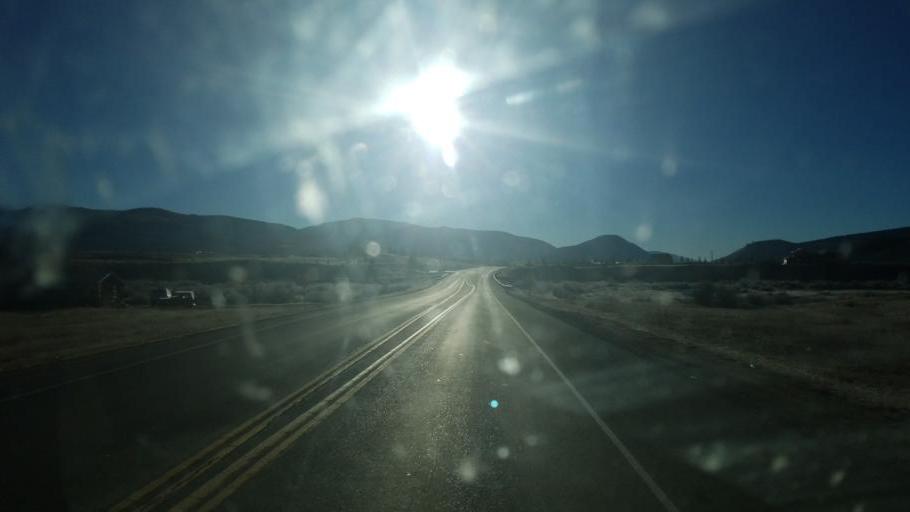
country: US
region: Colorado
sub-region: Gunnison County
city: Crested Butte
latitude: 38.8533
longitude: -106.9562
